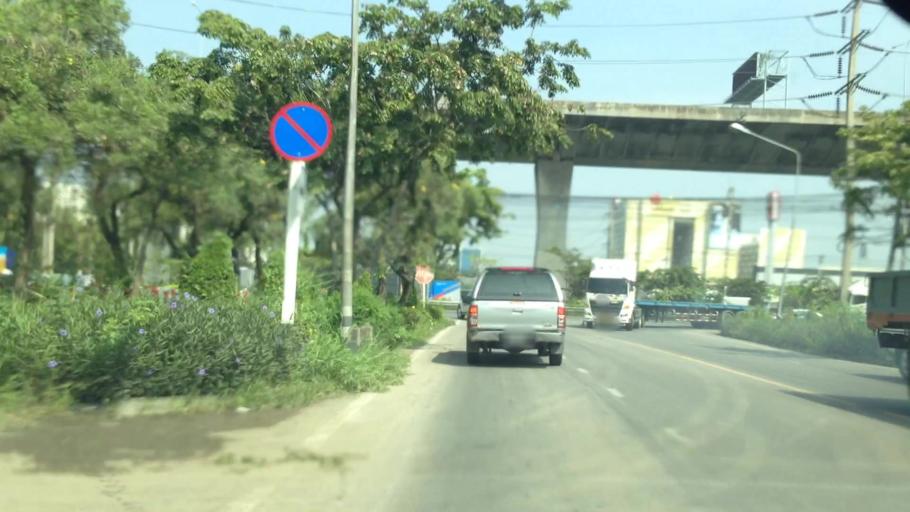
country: TH
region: Bangkok
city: Bang Na
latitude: 13.6647
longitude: 100.6454
